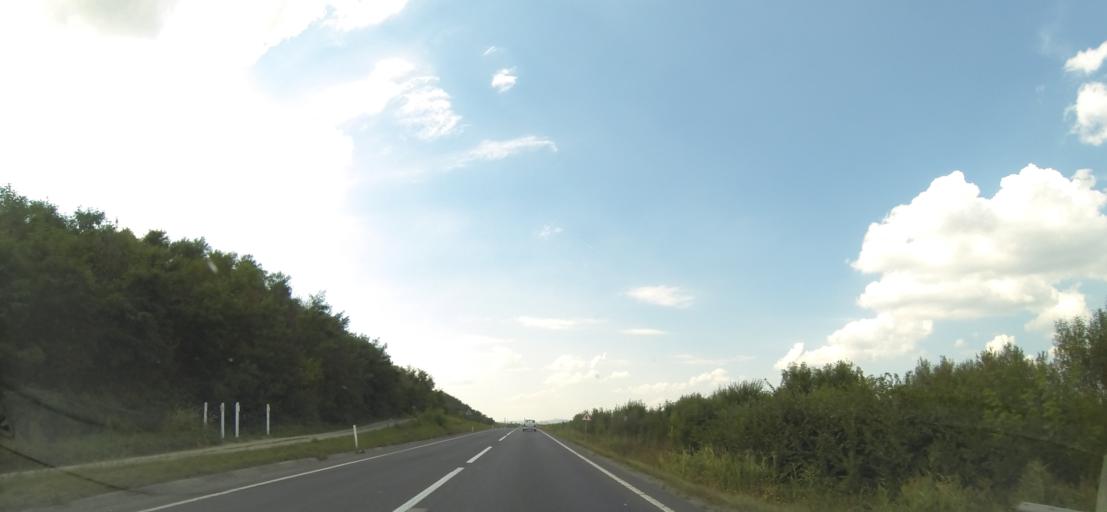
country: RO
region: Brasov
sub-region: Comuna Mandra
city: Mandra
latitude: 45.8220
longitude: 25.0698
